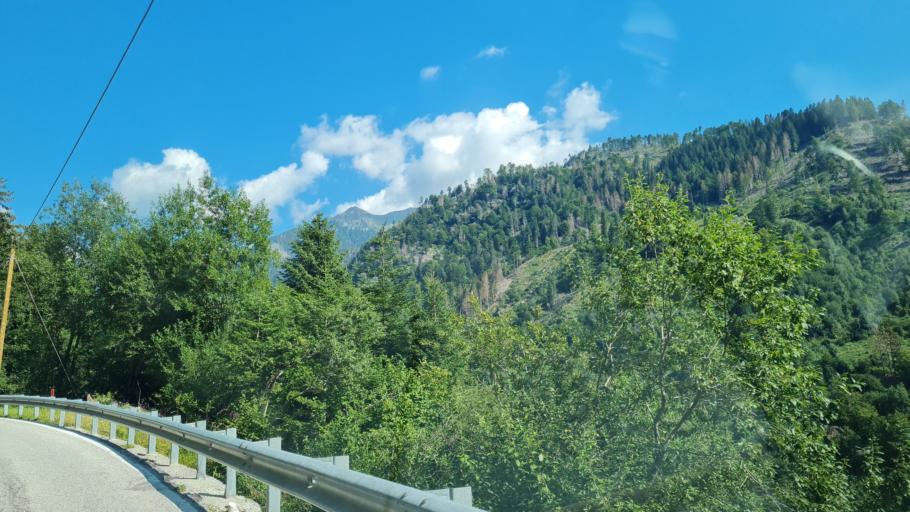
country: IT
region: Trentino-Alto Adige
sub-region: Provincia di Trento
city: Carzano
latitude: 46.1196
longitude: 11.4847
